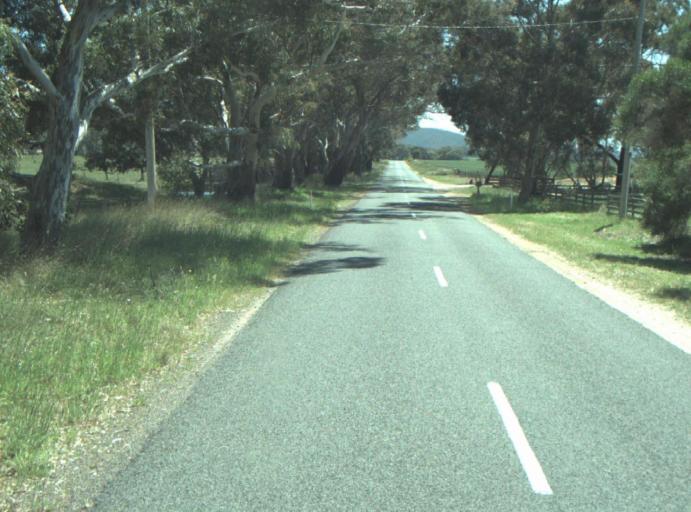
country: AU
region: Victoria
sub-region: Greater Geelong
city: Lara
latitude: -37.8648
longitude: 144.2789
